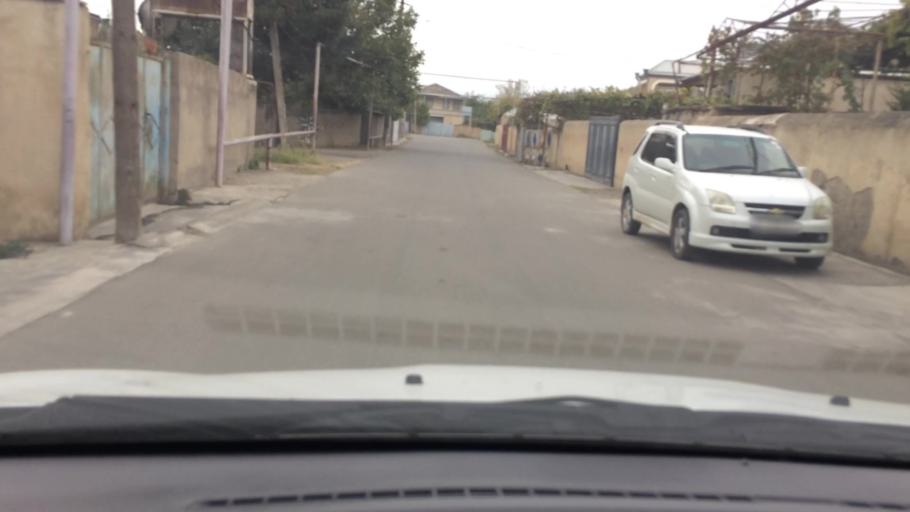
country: GE
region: Kvemo Kartli
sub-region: Marneuli
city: Marneuli
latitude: 41.4811
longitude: 44.7984
